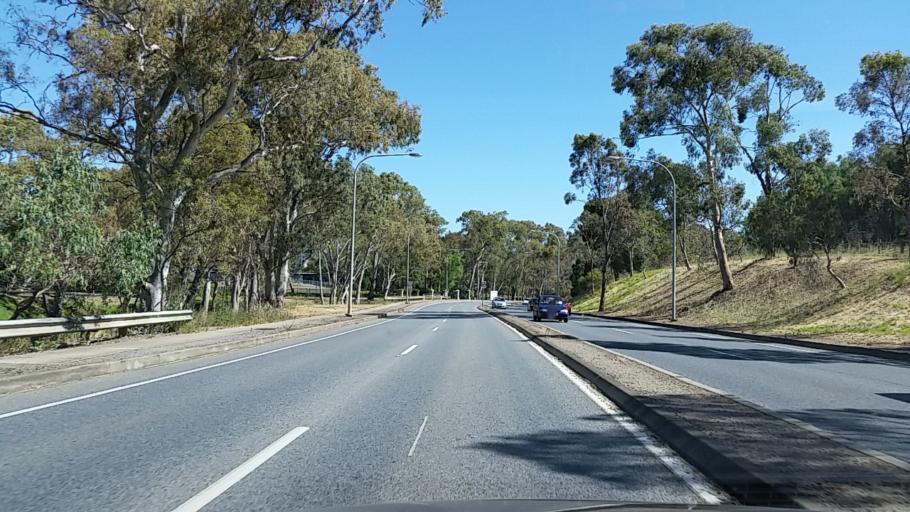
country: AU
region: South Australia
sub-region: Tea Tree Gully
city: Hope Valley
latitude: -34.8190
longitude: 138.6951
